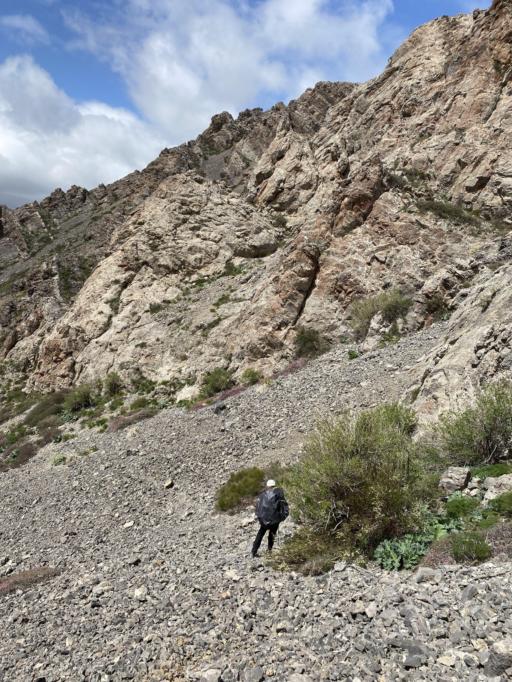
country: KZ
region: Ongtustik Qazaqstan
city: Ashchysay
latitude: 43.6394
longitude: 68.9266
